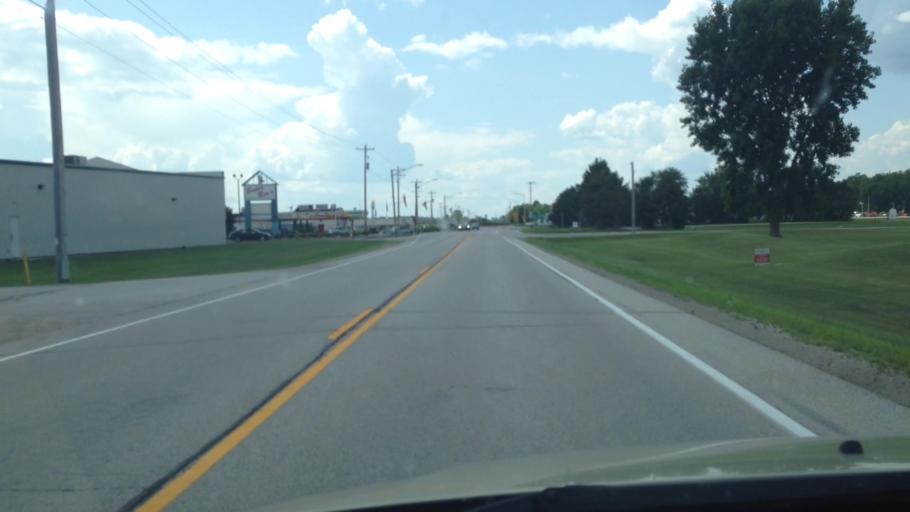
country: US
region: Wisconsin
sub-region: Brown County
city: Pulaski
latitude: 44.6573
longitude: -88.2175
